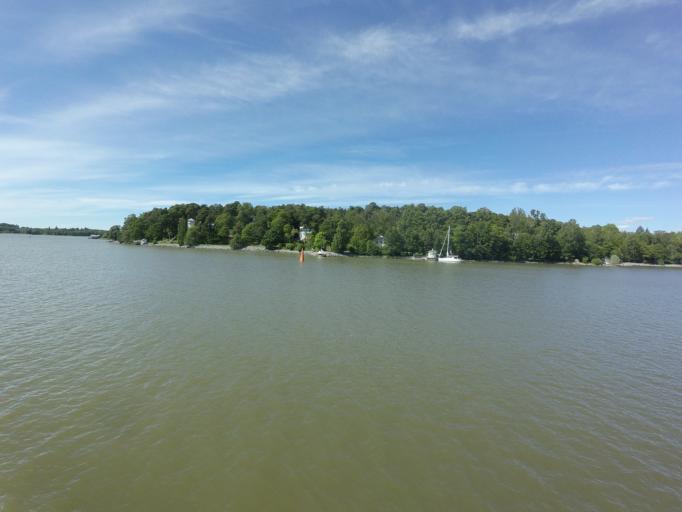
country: FI
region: Varsinais-Suomi
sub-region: Turku
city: Raisio
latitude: 60.4215
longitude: 22.1739
